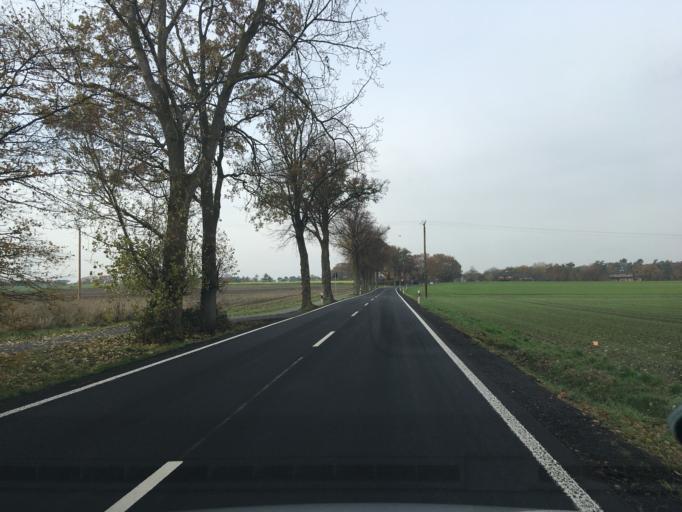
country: DE
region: North Rhine-Westphalia
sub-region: Regierungsbezirk Munster
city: Velen
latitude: 51.9138
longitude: 6.9648
